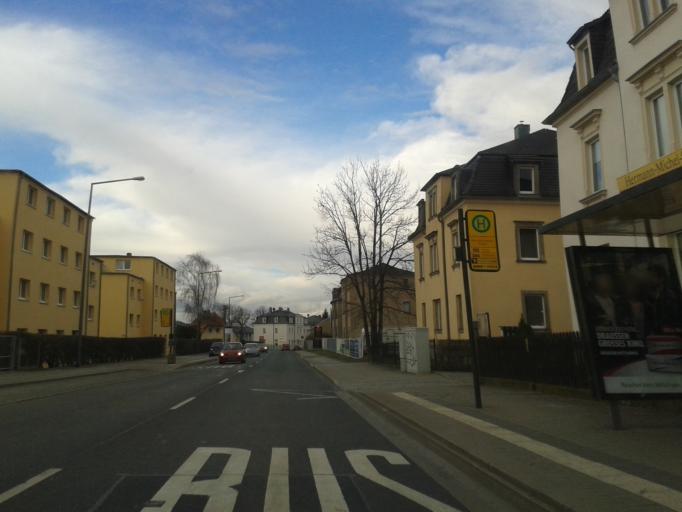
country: DE
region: Saxony
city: Bannewitz
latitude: 51.0057
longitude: 13.6885
